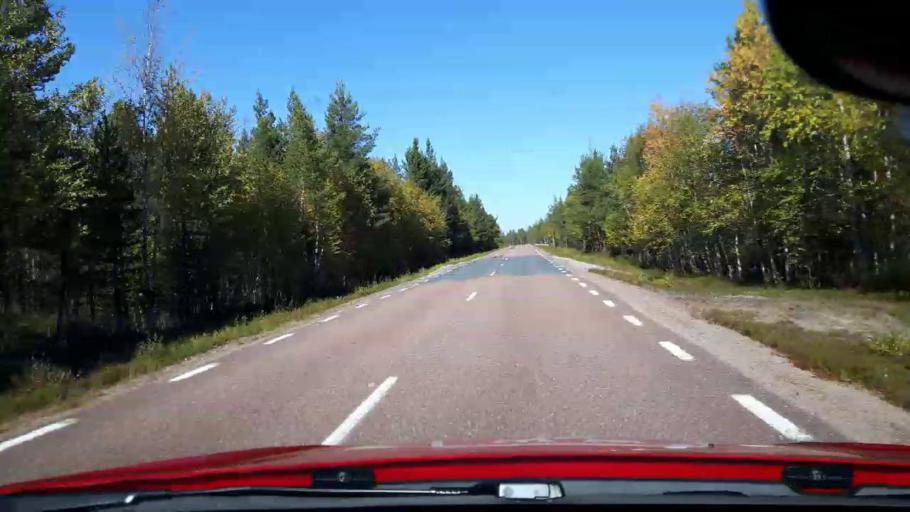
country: SE
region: Jaemtland
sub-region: Harjedalens Kommun
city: Sveg
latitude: 61.7361
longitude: 14.1635
